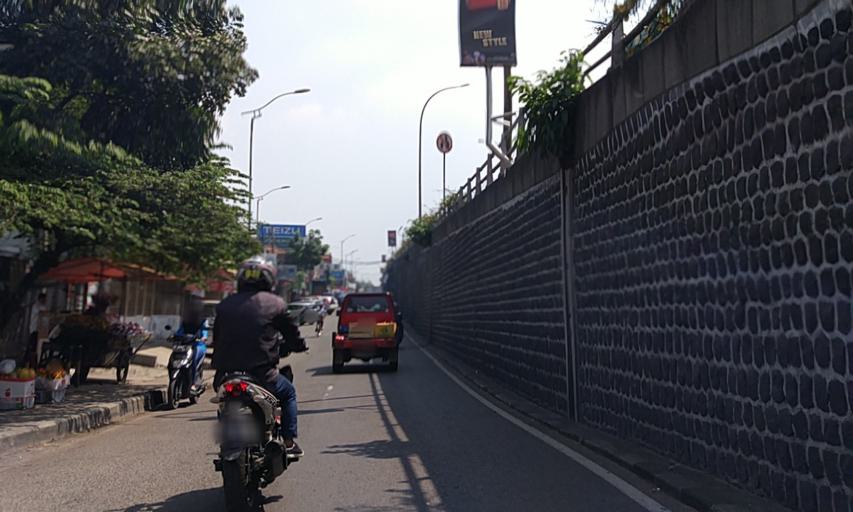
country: ID
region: West Java
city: Cimahi
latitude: -6.8981
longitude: 107.5614
